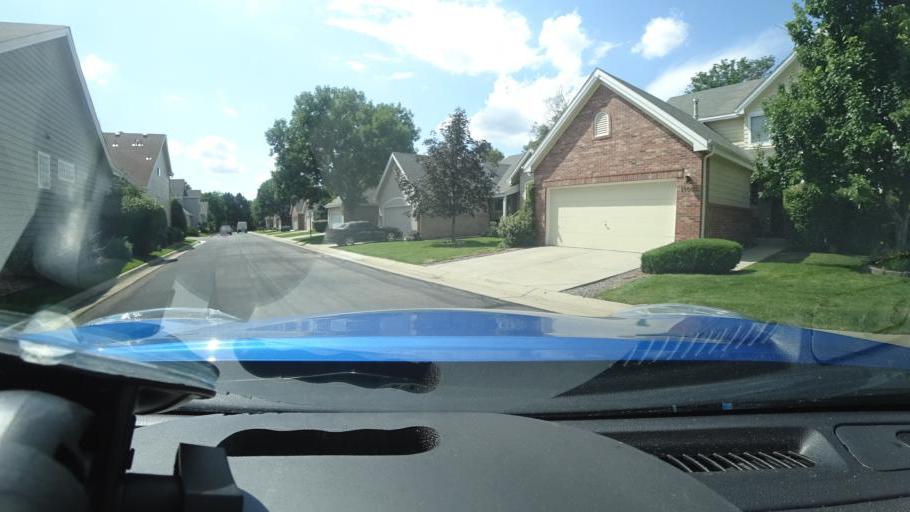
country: US
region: Colorado
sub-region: Adams County
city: Aurora
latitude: 39.6762
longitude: -104.8594
